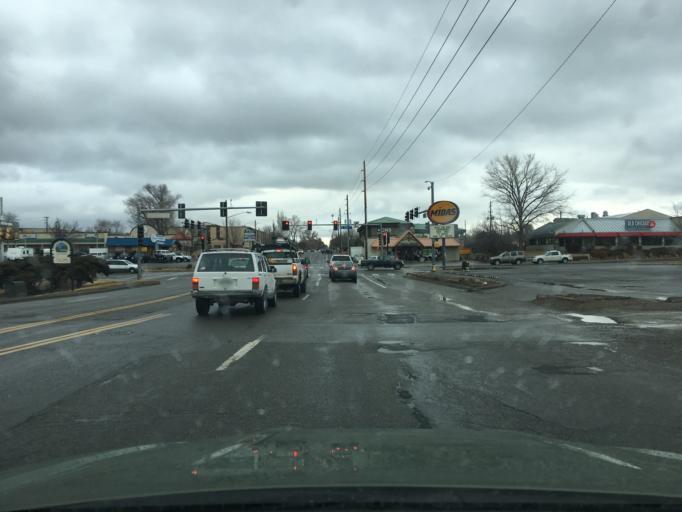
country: US
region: Colorado
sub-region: Mesa County
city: Grand Junction
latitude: 39.0768
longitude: -108.5708
